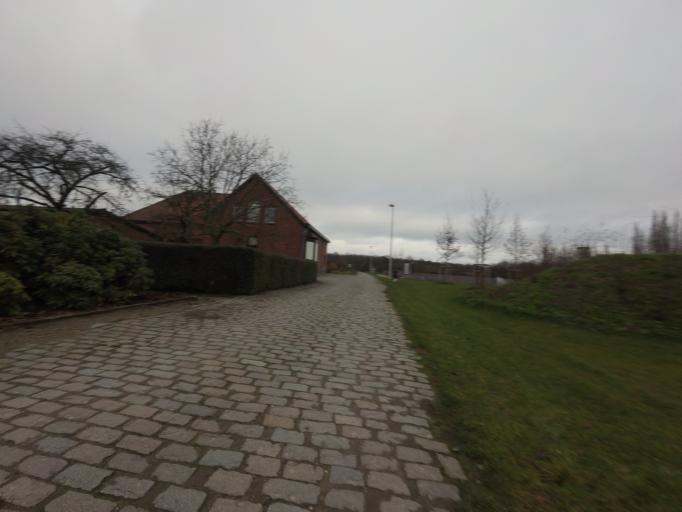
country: BE
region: Flanders
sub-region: Provincie Antwerpen
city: Aartselaar
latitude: 51.1592
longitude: 4.3771
